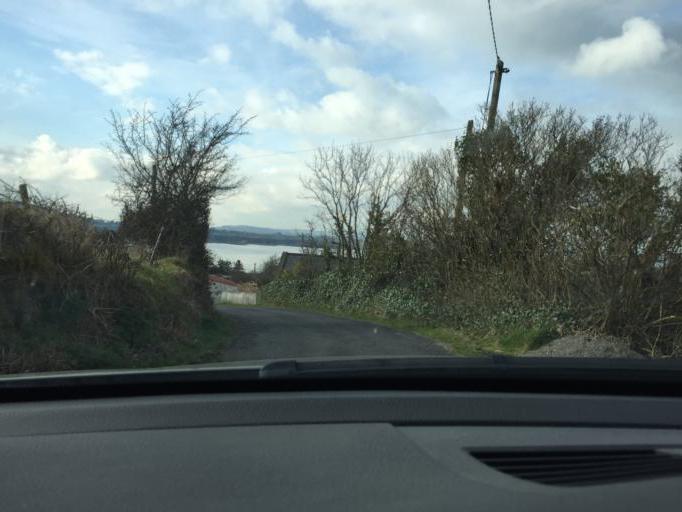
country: IE
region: Leinster
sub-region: Wicklow
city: Valleymount
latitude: 53.0930
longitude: -6.5240
